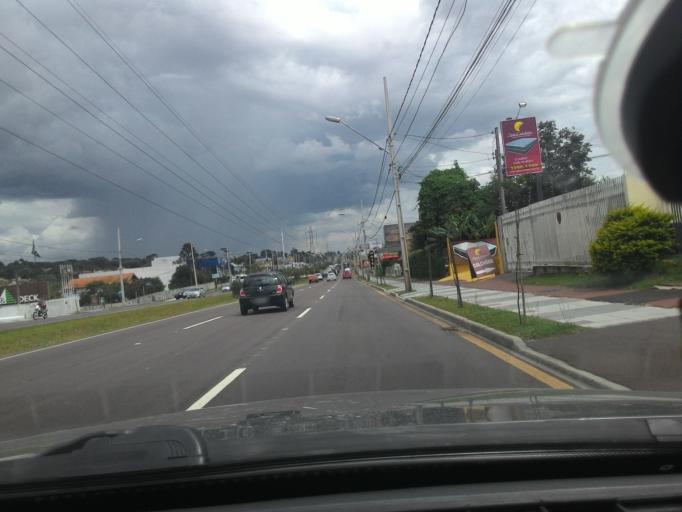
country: BR
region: Parana
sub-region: Pinhais
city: Pinhais
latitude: -25.4734
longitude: -49.2285
